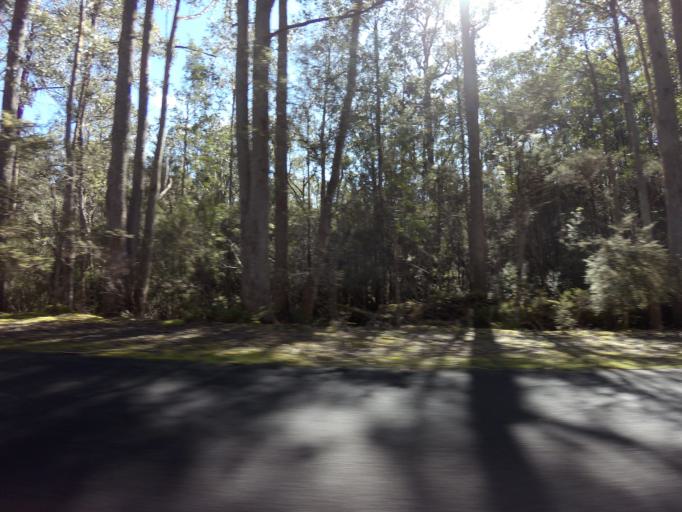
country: AU
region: Tasmania
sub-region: Derwent Valley
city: New Norfolk
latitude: -42.7340
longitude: 146.4821
